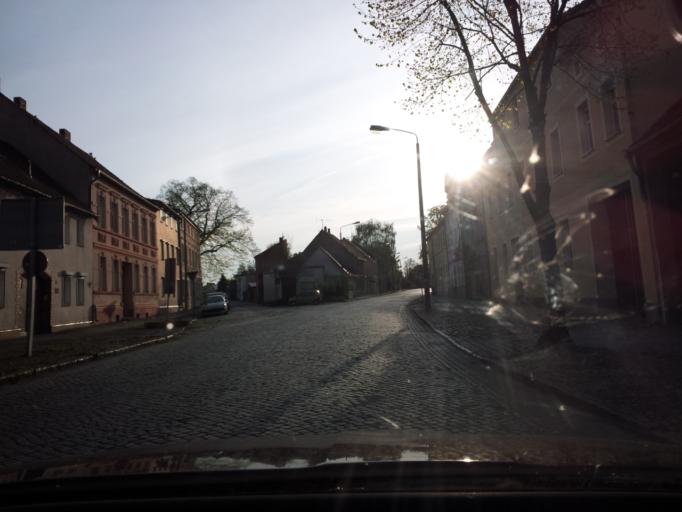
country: DE
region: Brandenburg
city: Dahme
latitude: 51.8684
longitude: 13.4197
